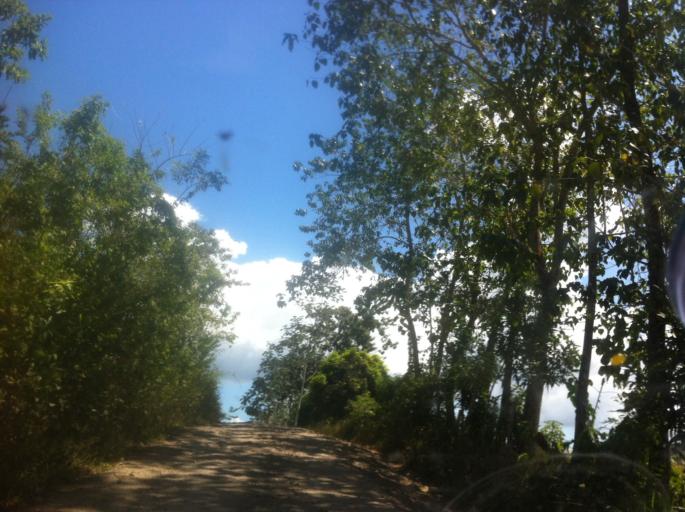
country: NI
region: Rio San Juan
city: San Carlos
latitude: 11.2391
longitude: -84.5115
